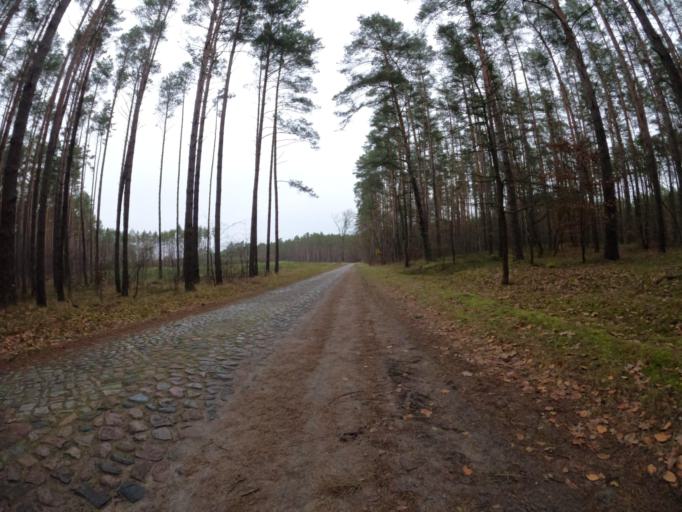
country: PL
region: West Pomeranian Voivodeship
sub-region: Powiat mysliborski
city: Debno
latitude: 52.7119
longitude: 14.7229
